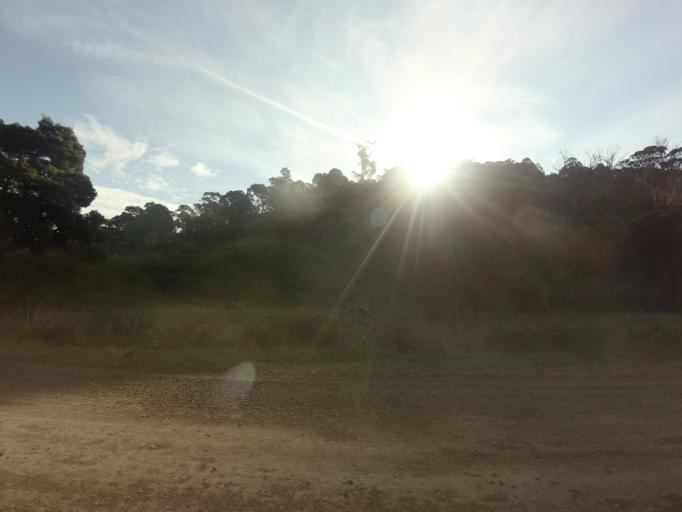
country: AU
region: Tasmania
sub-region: Brighton
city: Bridgewater
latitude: -42.5106
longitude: 147.4268
